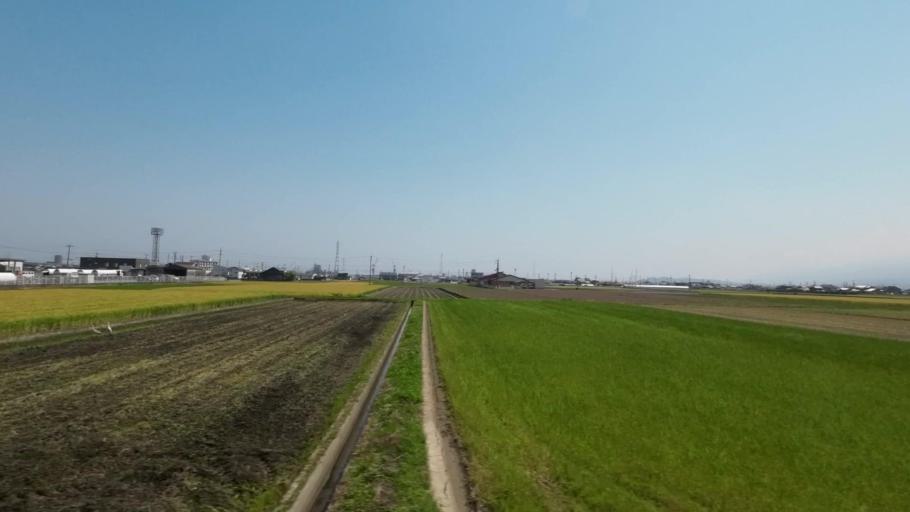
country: JP
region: Ehime
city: Saijo
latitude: 33.9169
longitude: 133.0970
